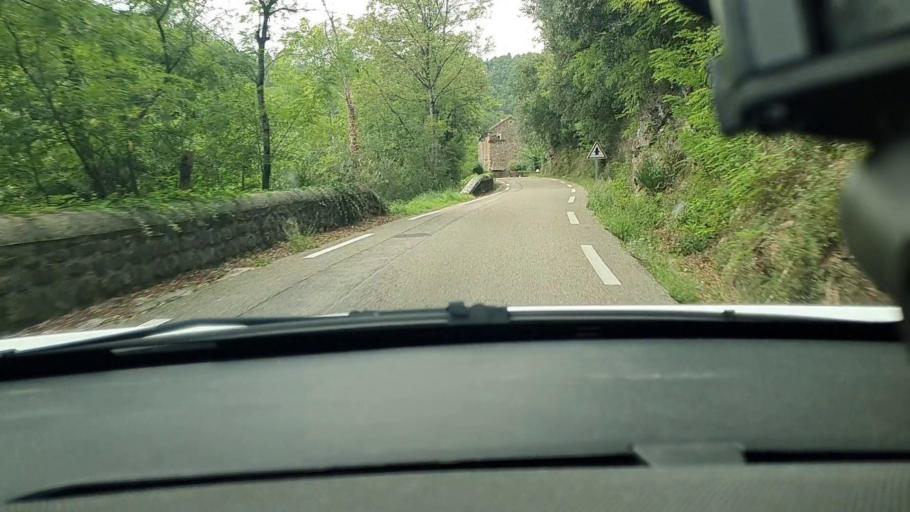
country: FR
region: Languedoc-Roussillon
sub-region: Departement du Gard
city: Branoux-les-Taillades
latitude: 44.3044
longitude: 3.9920
